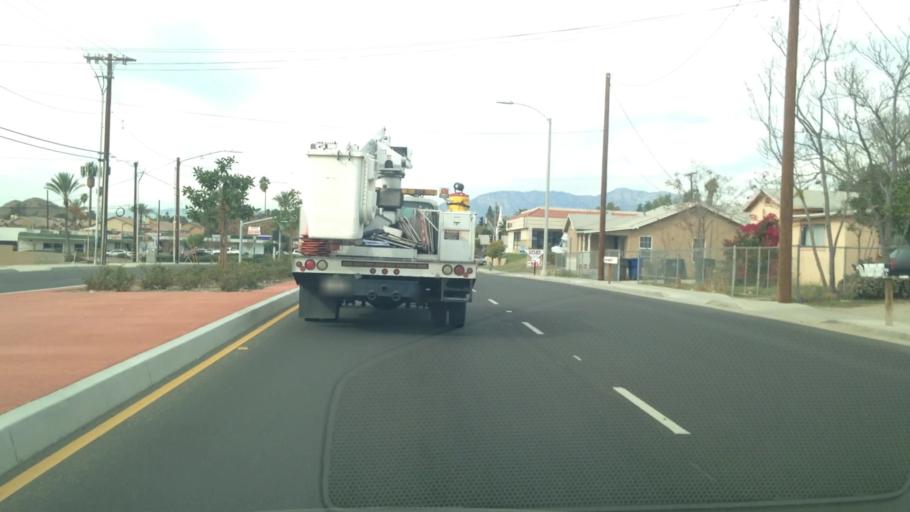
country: US
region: California
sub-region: Riverside County
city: Pedley
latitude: 33.9270
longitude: -117.4734
